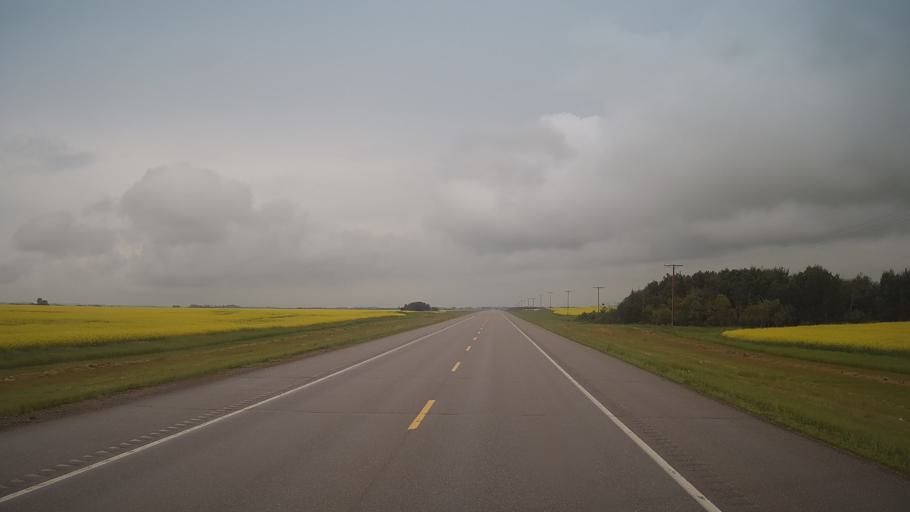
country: CA
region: Saskatchewan
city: Wilkie
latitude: 52.4261
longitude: -108.9090
